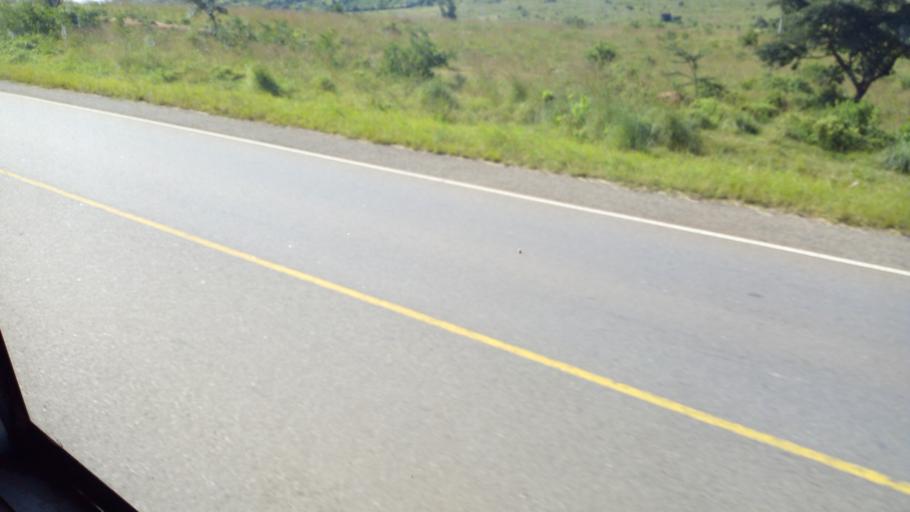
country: UG
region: Central Region
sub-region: Lyantonde District
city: Lyantonde
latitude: -0.4494
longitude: 31.0610
